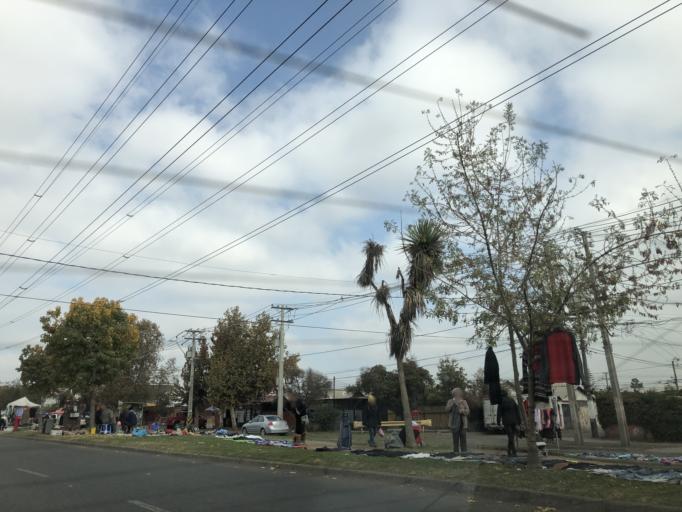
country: CL
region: Santiago Metropolitan
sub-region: Provincia de Cordillera
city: Puente Alto
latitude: -33.5826
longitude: -70.5974
